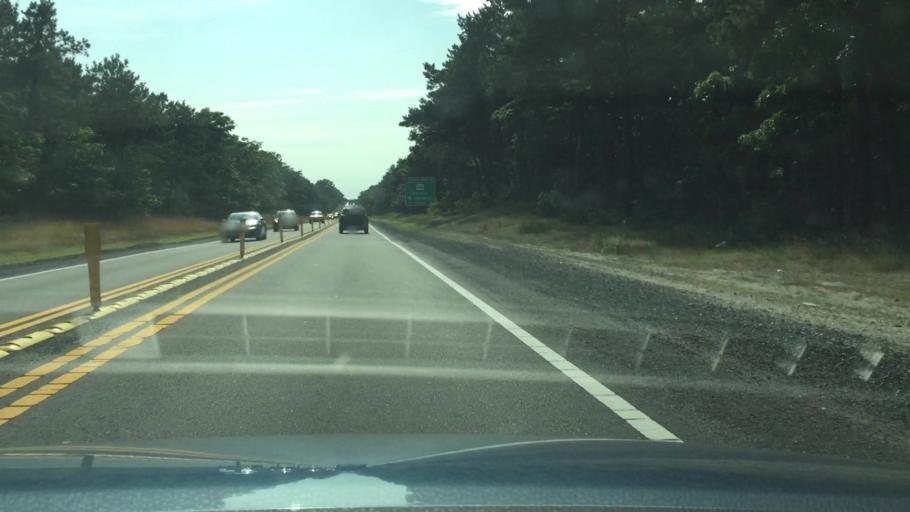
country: US
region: Massachusetts
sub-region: Barnstable County
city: Northwest Harwich
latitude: 41.7008
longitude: -70.1237
